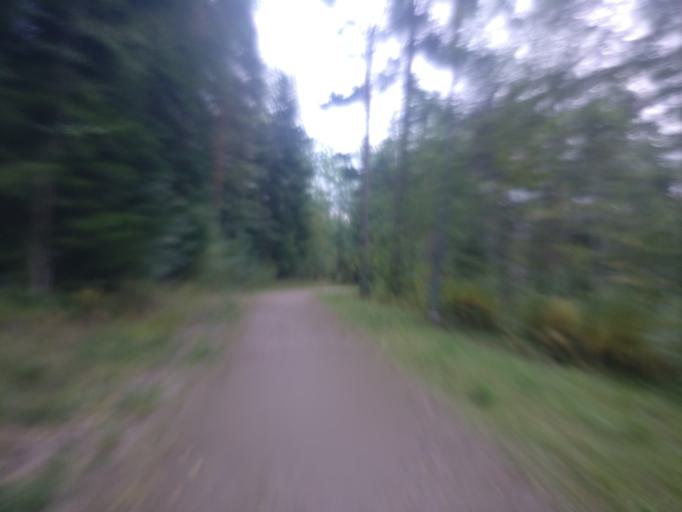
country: SE
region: Vaesternorrland
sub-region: Sundsvalls Kommun
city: Stockvik
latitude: 62.3548
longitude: 17.3698
